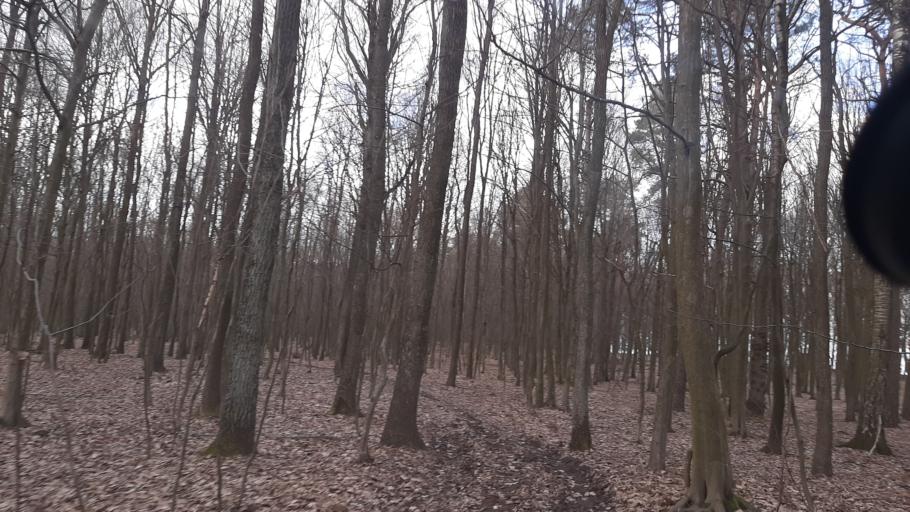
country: PL
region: Lublin Voivodeship
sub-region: Powiat lubelski
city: Jastkow
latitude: 51.3707
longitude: 22.4152
